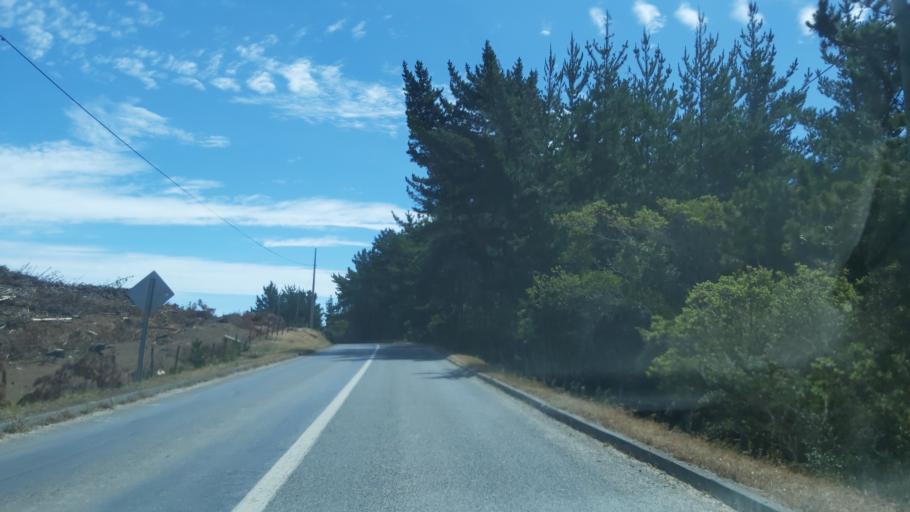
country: CL
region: Maule
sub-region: Provincia de Talca
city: Constitucion
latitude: -35.5394
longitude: -72.5543
